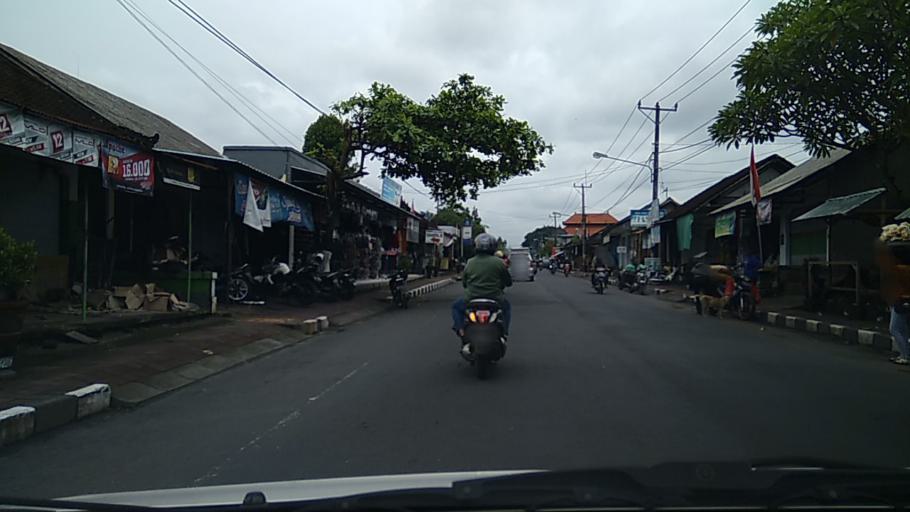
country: ID
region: Bali
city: Banjar Kembangsari
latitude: -8.5161
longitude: 115.2098
